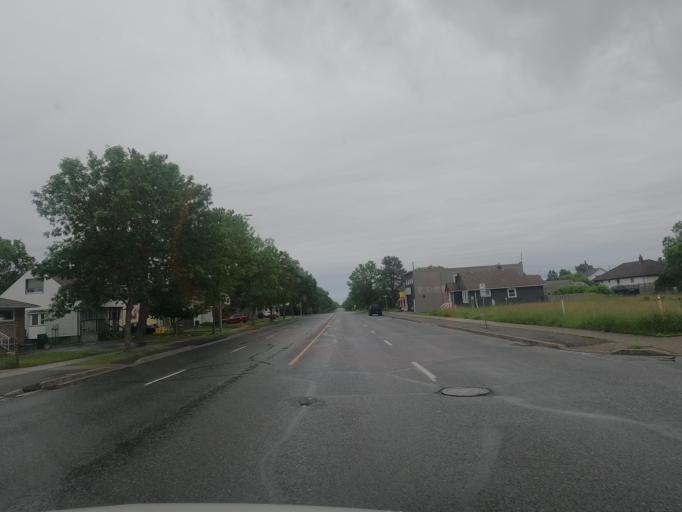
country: CA
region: Ontario
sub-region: Thunder Bay District
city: Thunder Bay
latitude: 48.4680
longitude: -89.1823
